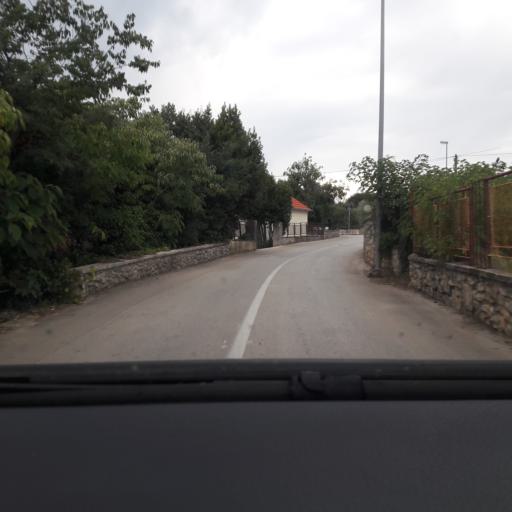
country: HR
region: Zadarska
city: Zadar
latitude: 44.1538
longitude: 15.2043
